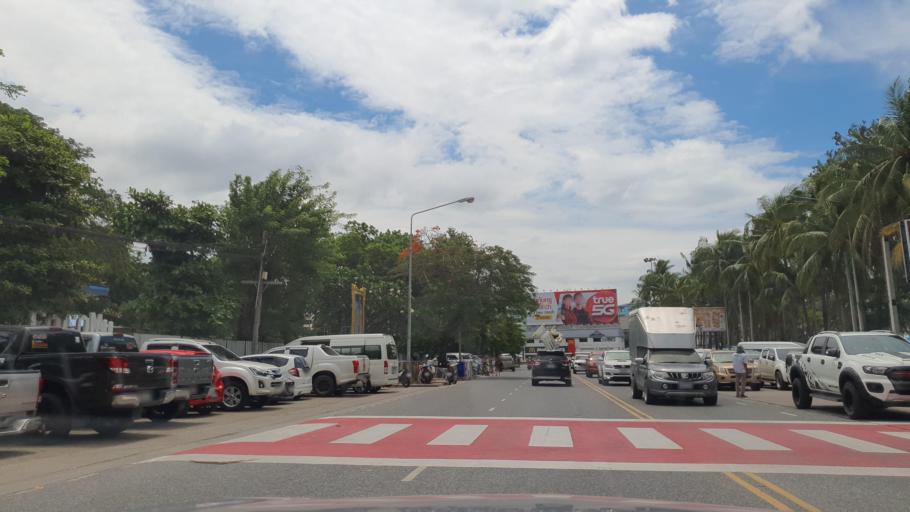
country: TH
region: Chon Buri
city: Chon Buri
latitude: 13.2851
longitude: 100.9146
